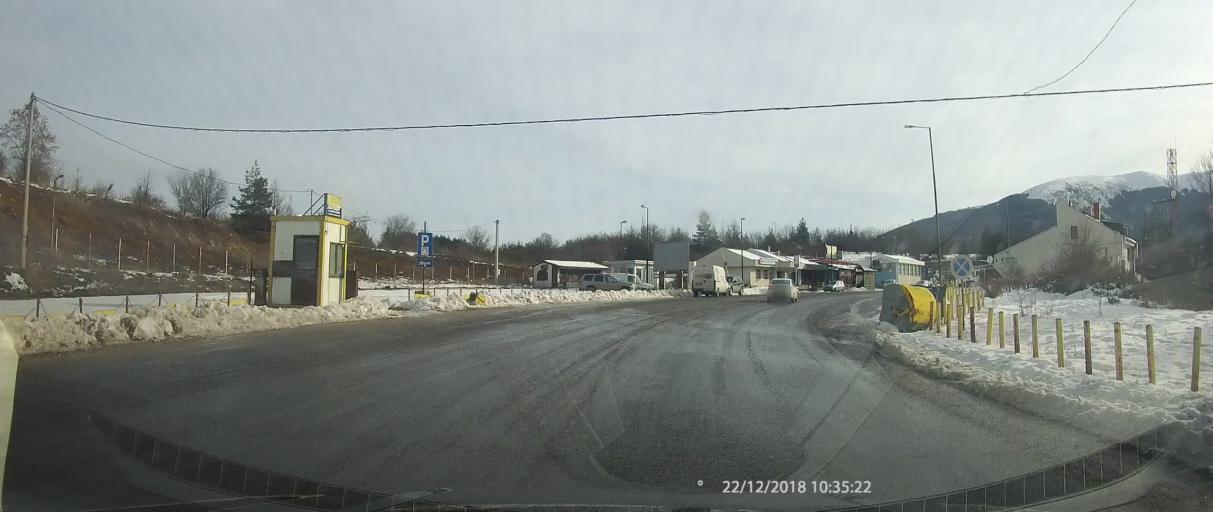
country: MK
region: Kriva Palanka
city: Kriva Palanka
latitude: 42.2220
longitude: 22.4555
